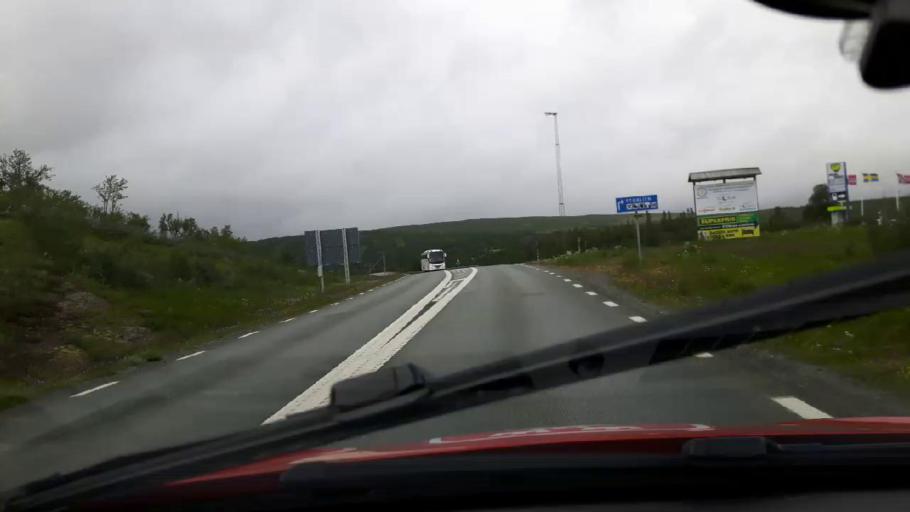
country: NO
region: Nord-Trondelag
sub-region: Meraker
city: Meraker
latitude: 63.3086
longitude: 12.1081
